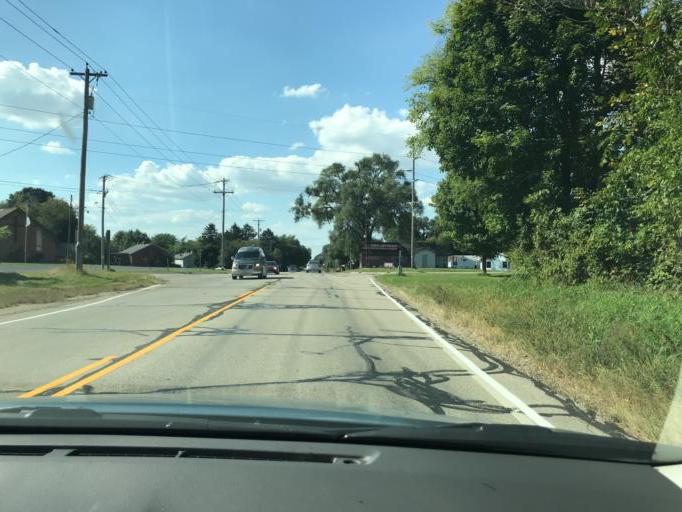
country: US
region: Wisconsin
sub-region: Walworth County
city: Williams Bay
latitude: 42.6087
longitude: -88.5597
